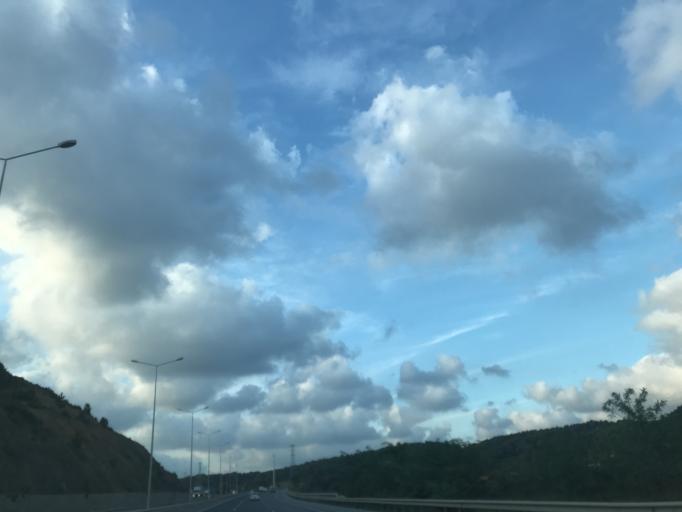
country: TR
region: Istanbul
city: Kemerburgaz
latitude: 41.1928
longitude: 28.8686
